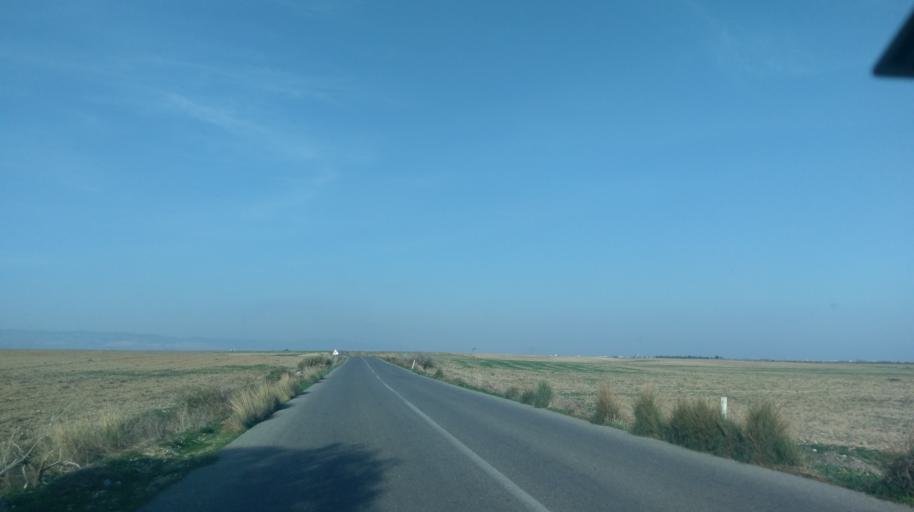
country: CY
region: Ammochostos
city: Achna
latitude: 35.1366
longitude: 33.7420
